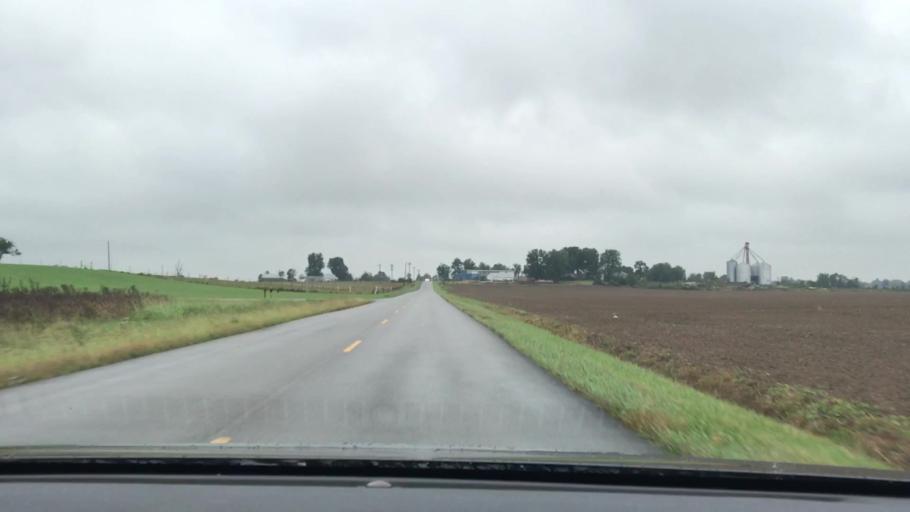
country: US
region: Kentucky
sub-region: Hopkins County
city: Madisonville
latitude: 37.3762
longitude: -87.3479
